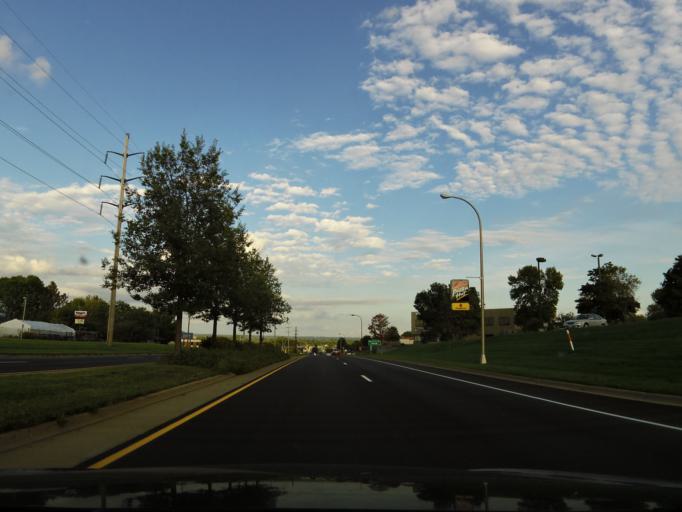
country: US
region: Minnesota
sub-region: Dakota County
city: Hastings
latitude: 44.7383
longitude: -92.8796
